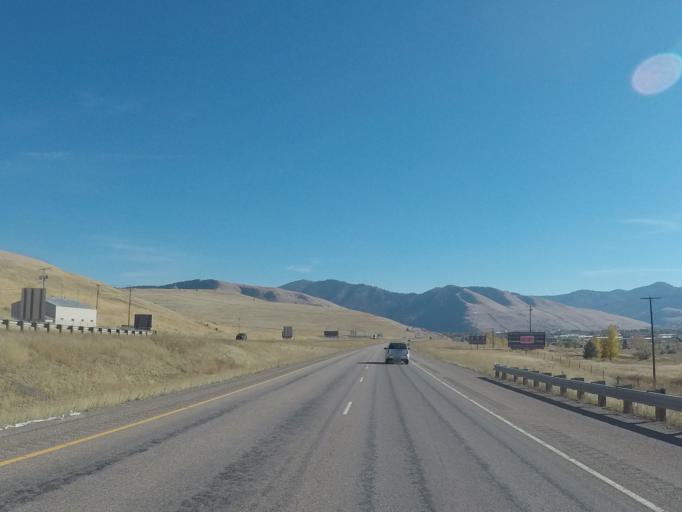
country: US
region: Montana
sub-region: Missoula County
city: Missoula
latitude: 46.9034
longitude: -114.0206
